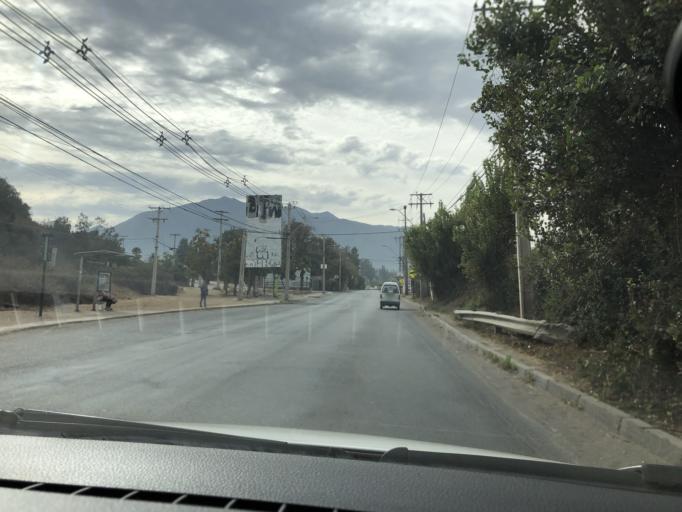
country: CL
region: Santiago Metropolitan
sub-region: Provincia de Cordillera
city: Puente Alto
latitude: -33.6112
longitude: -70.5424
